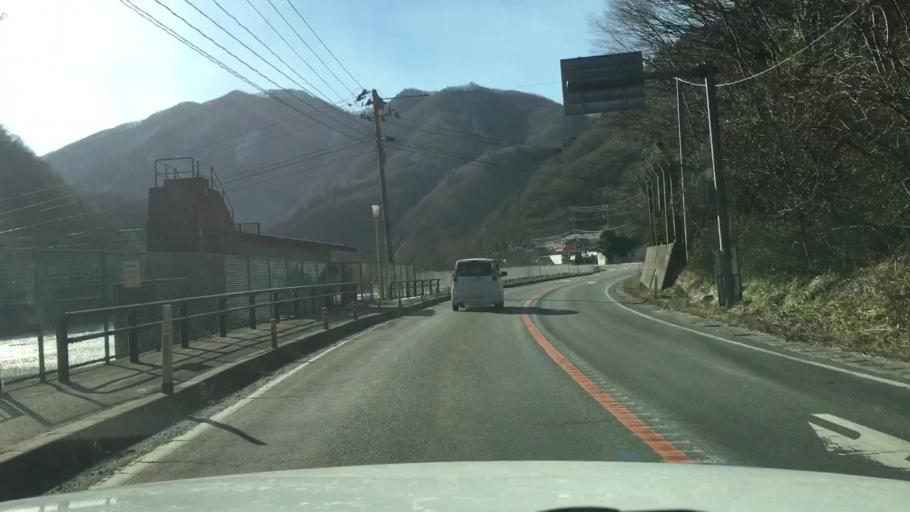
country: JP
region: Iwate
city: Miyako
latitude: 39.5930
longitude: 141.6742
